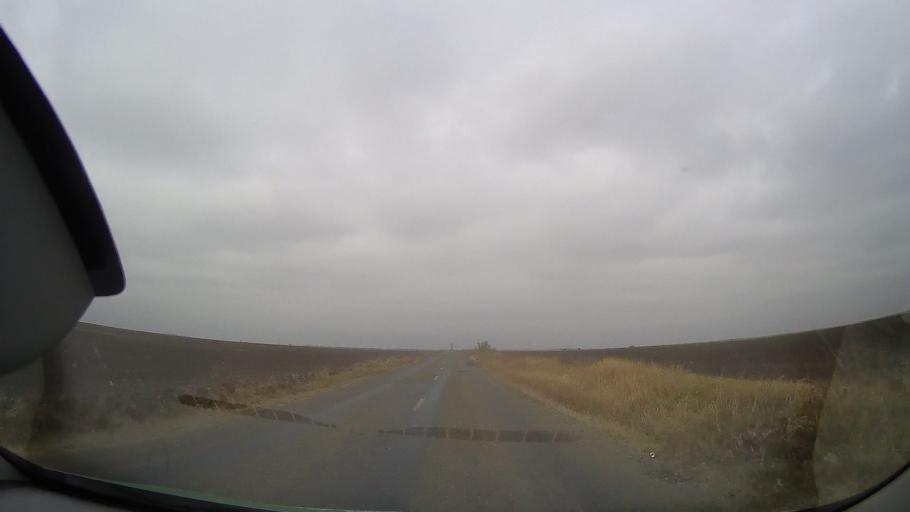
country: RO
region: Buzau
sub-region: Comuna Bradeanu
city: Bradeanu
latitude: 44.8934
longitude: 26.8737
